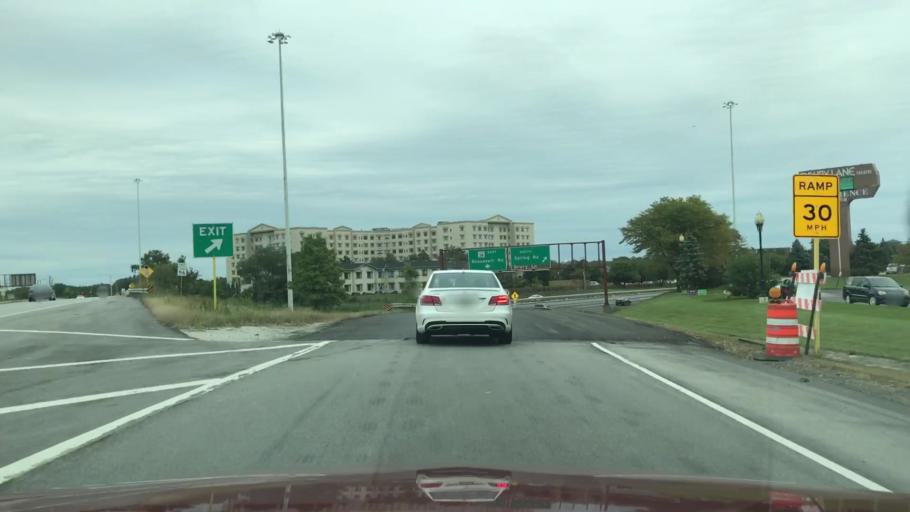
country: US
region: Illinois
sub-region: DuPage County
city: Oakbrook Terrace
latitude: 41.8599
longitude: -87.9544
